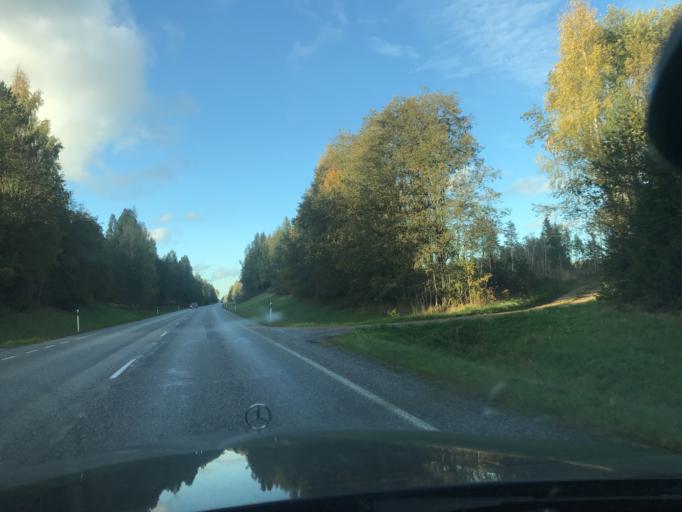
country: RU
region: Pskov
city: Pechory
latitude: 57.6591
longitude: 27.3316
